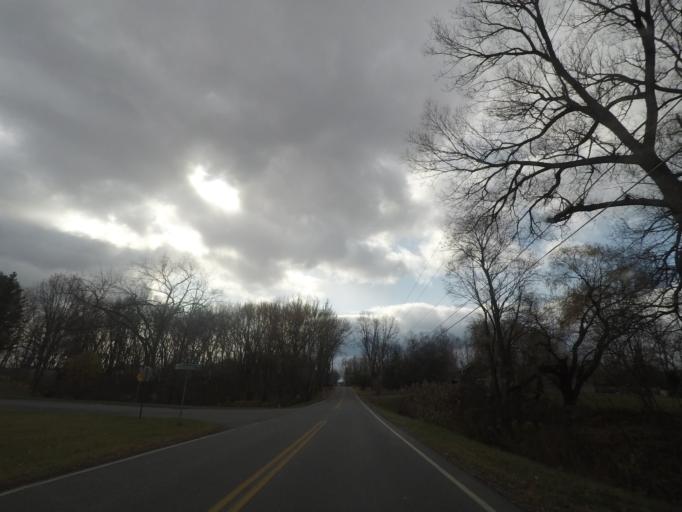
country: US
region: New York
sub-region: Saratoga County
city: Ballston Spa
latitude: 42.9913
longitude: -73.8167
